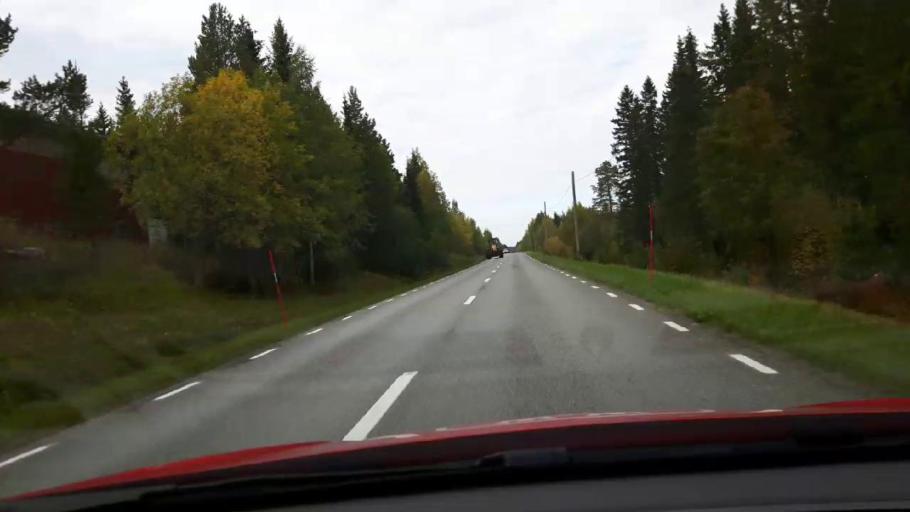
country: SE
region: Jaemtland
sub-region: Krokoms Kommun
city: Krokom
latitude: 63.1888
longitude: 14.0640
